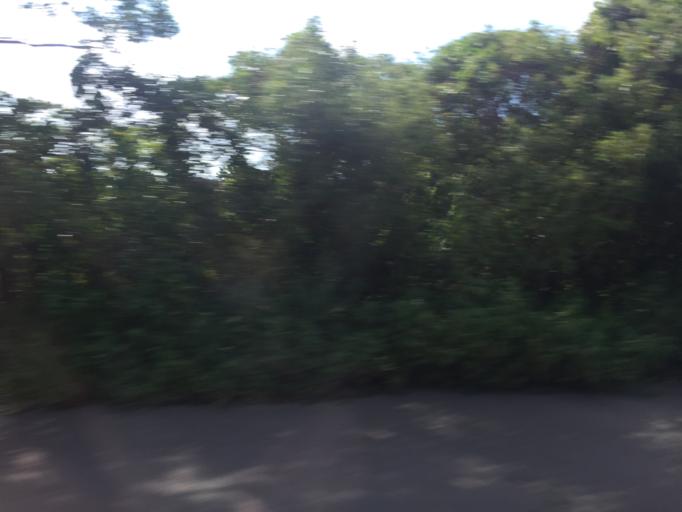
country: TW
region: Taiwan
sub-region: Hsinchu
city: Hsinchu
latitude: 24.6990
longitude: 120.8875
